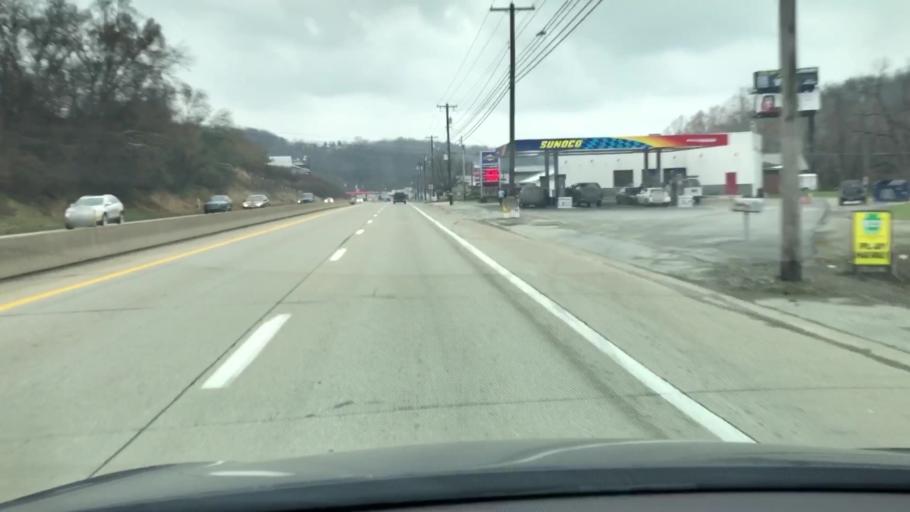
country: US
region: Pennsylvania
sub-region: Westmoreland County
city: Scottdale
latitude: 40.0608
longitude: -79.5629
